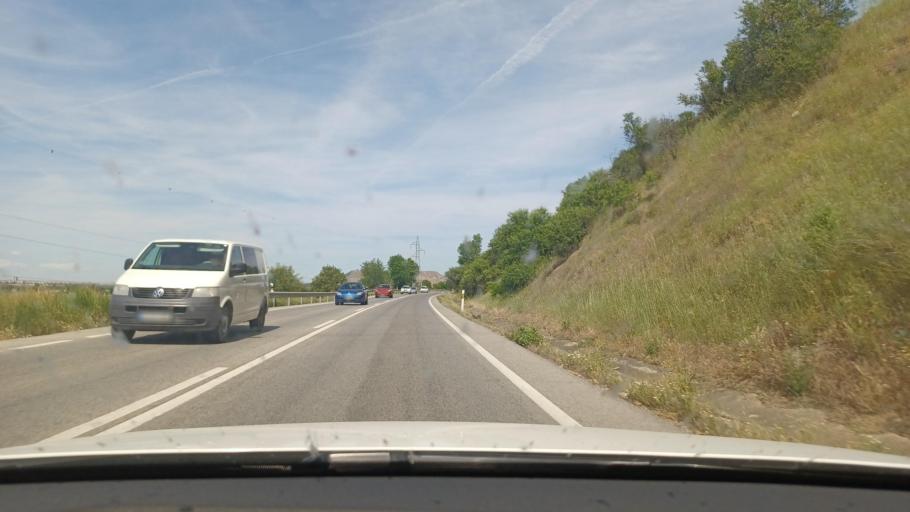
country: ES
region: Madrid
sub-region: Provincia de Madrid
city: Mejorada del Campo
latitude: 40.4186
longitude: -3.4701
